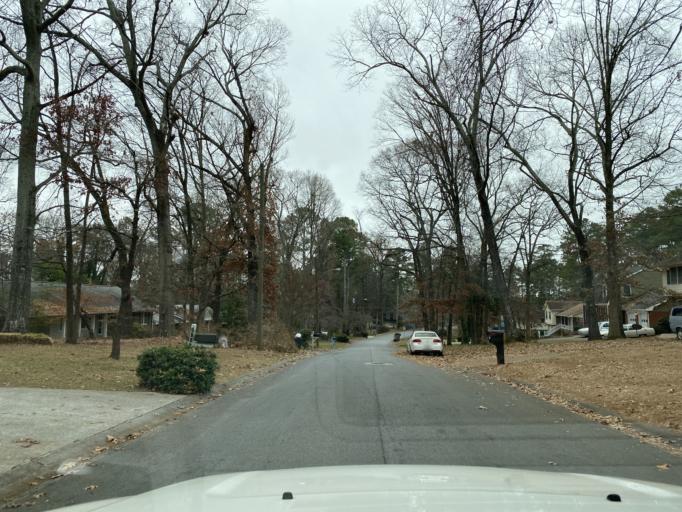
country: US
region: Georgia
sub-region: Cobb County
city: Fair Oaks
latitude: 33.9119
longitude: -84.5844
